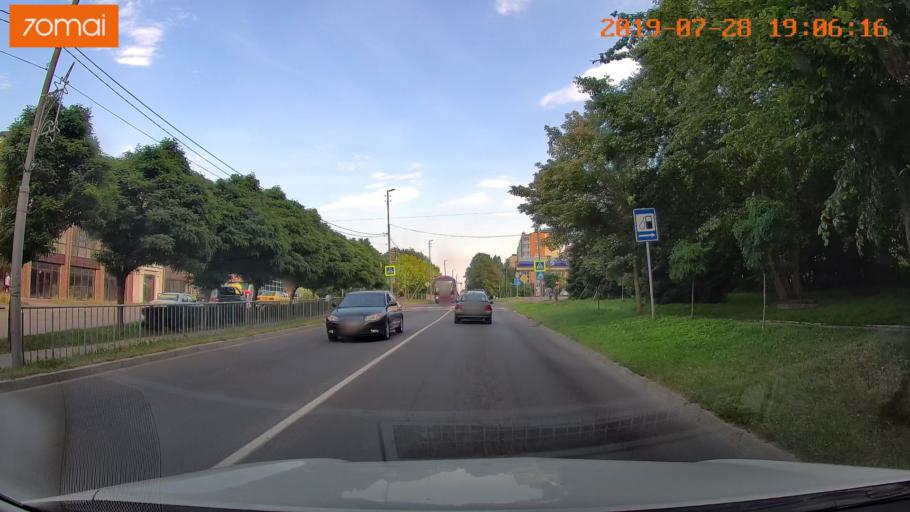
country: RU
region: Kaliningrad
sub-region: Gorod Svetlogorsk
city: Svetlogorsk
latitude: 54.9315
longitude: 20.1647
